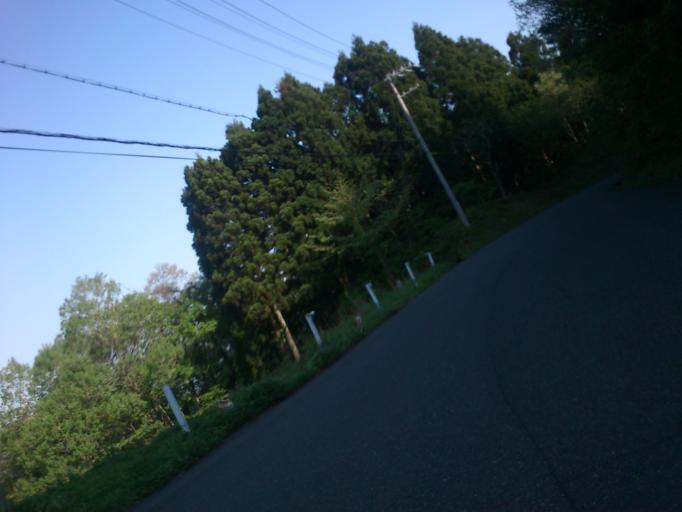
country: JP
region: Kyoto
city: Miyazu
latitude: 35.7157
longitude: 135.1952
